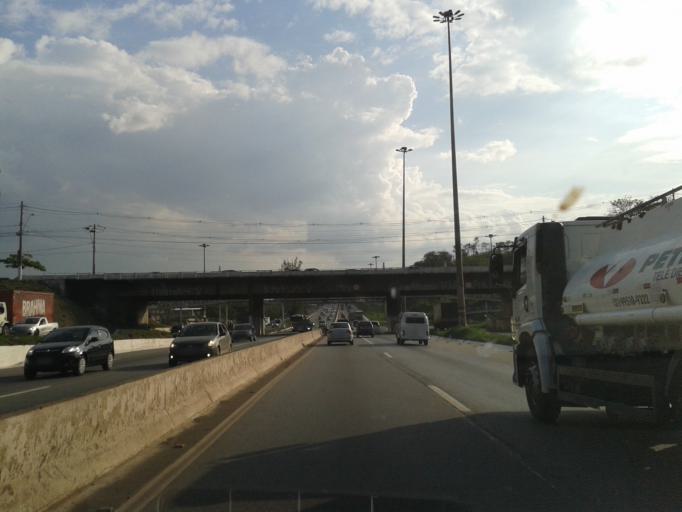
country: BR
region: Minas Gerais
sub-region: Belo Horizonte
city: Belo Horizonte
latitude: -19.8866
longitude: -43.9684
